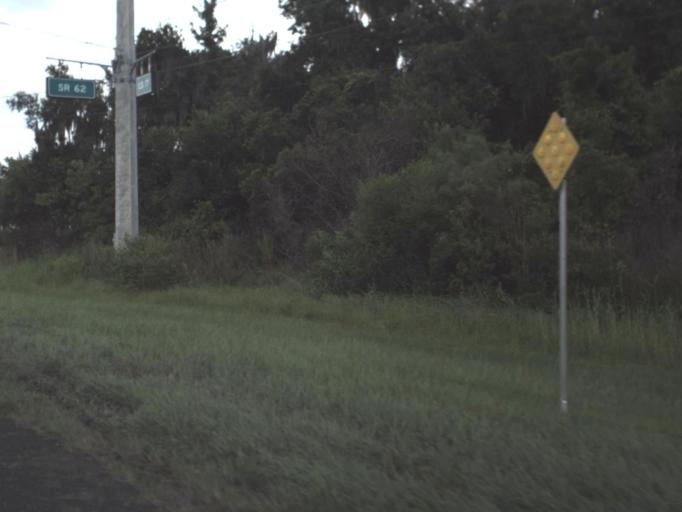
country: US
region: Florida
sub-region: Hardee County
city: Bowling Green
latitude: 27.5949
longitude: -81.8219
